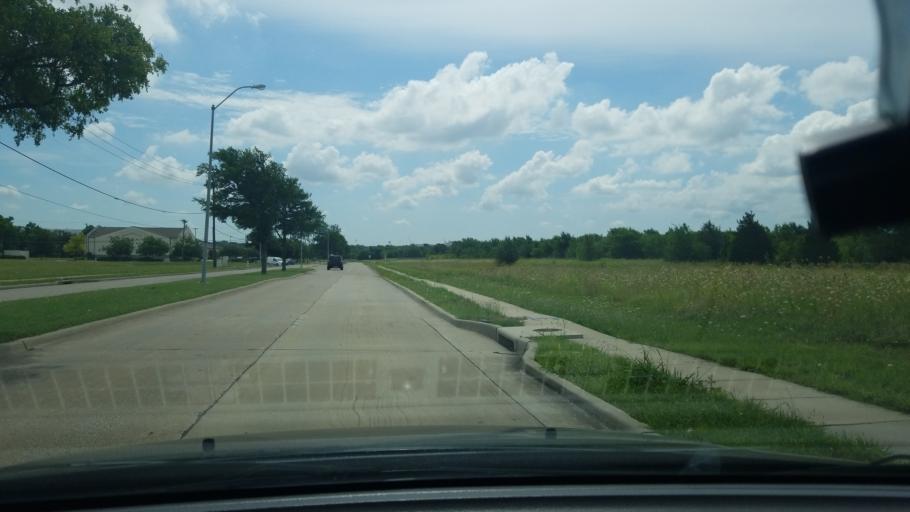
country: US
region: Texas
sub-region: Dallas County
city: Mesquite
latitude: 32.7703
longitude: -96.5818
